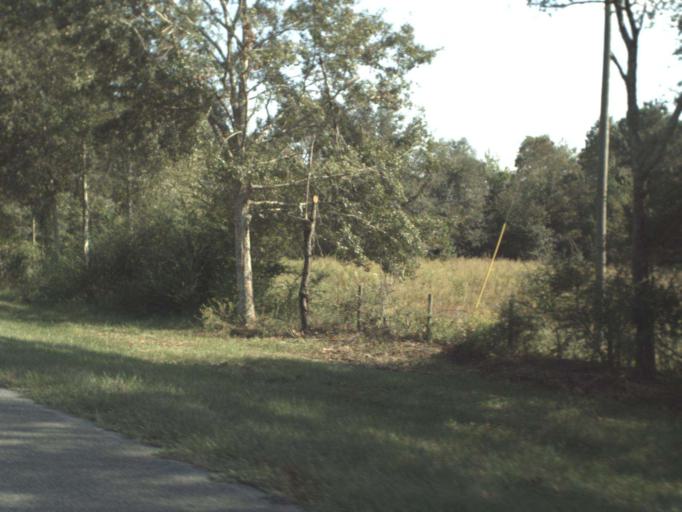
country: US
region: Florida
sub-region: Jackson County
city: Graceville
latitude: 30.9465
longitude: -85.6490
